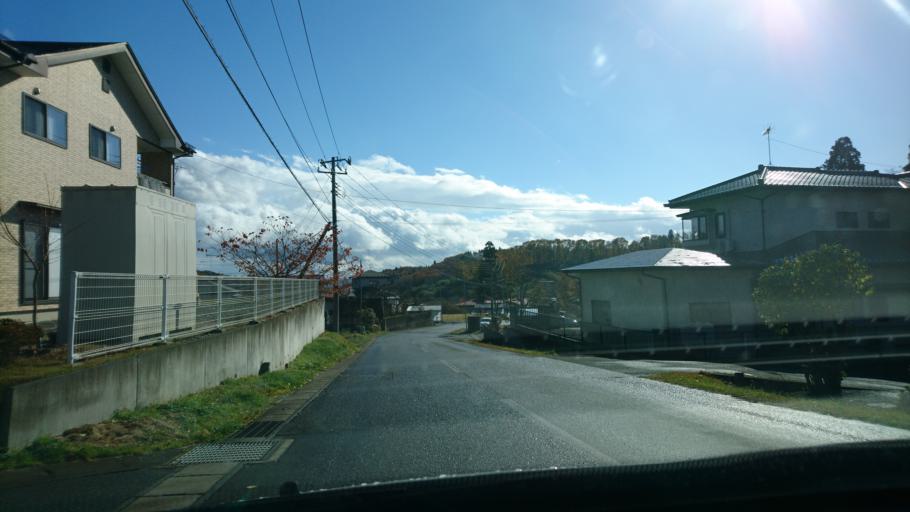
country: JP
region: Iwate
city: Ichinoseki
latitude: 38.9480
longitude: 141.1075
